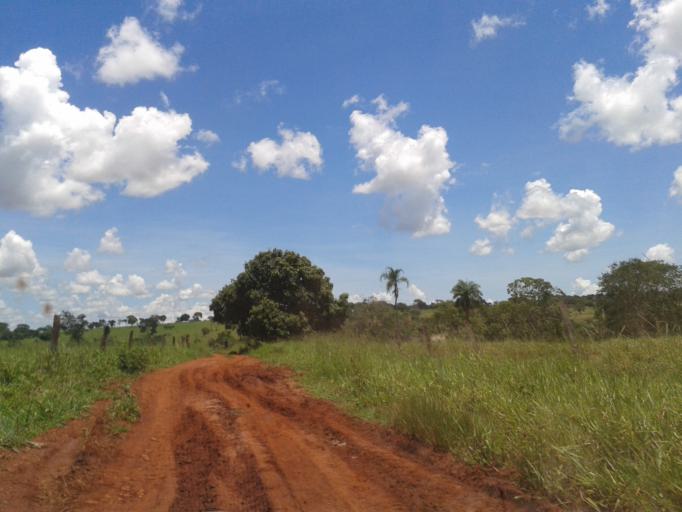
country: BR
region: Minas Gerais
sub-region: Santa Vitoria
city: Santa Vitoria
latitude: -18.7924
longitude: -49.8637
